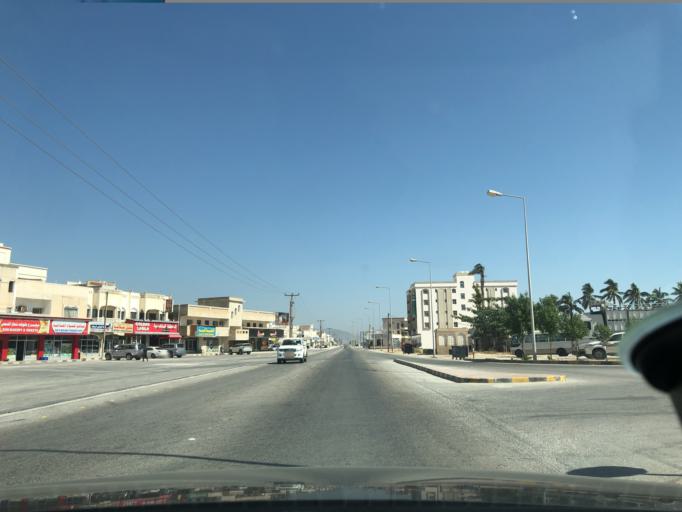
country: OM
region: Zufar
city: Salalah
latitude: 17.0195
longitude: 54.1602
